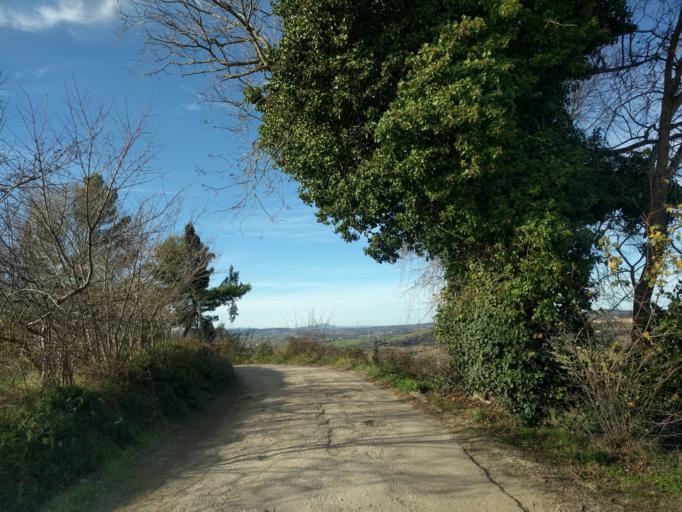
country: IT
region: The Marches
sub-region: Provincia di Pesaro e Urbino
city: Cuccurano
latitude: 43.8100
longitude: 12.9543
